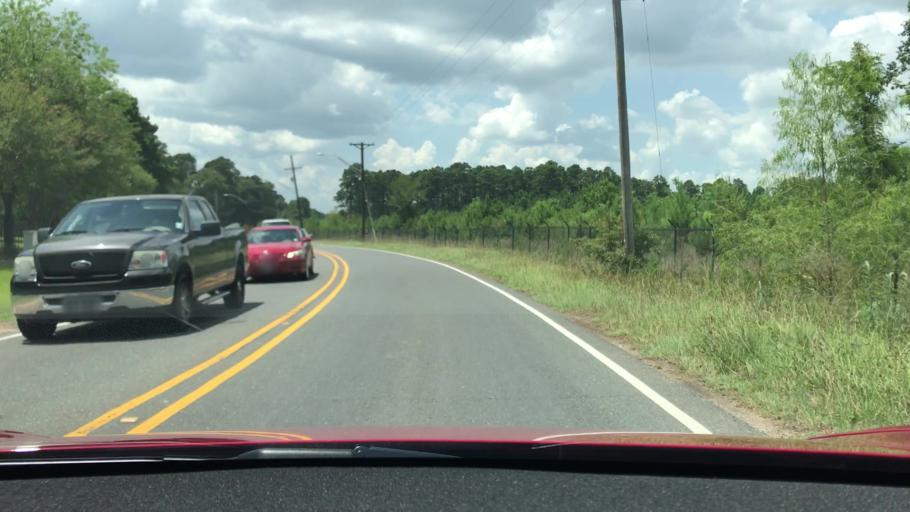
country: US
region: Louisiana
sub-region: Bossier Parish
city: Bossier City
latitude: 32.3838
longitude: -93.7139
